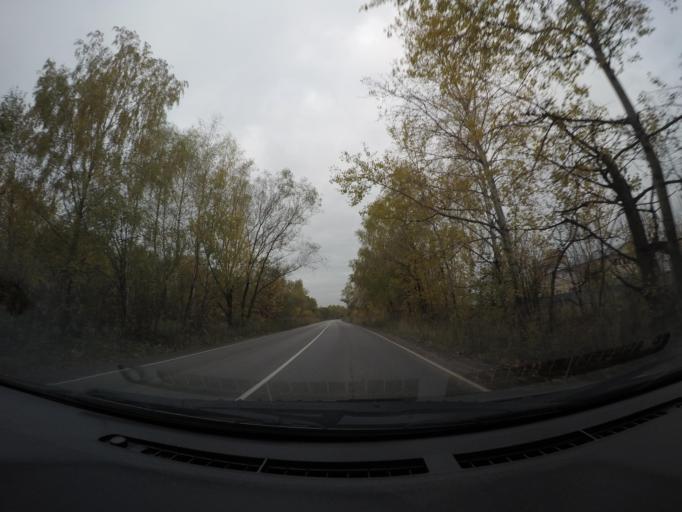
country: RU
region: Moskovskaya
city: Elektrougli
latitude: 55.7450
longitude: 38.2612
